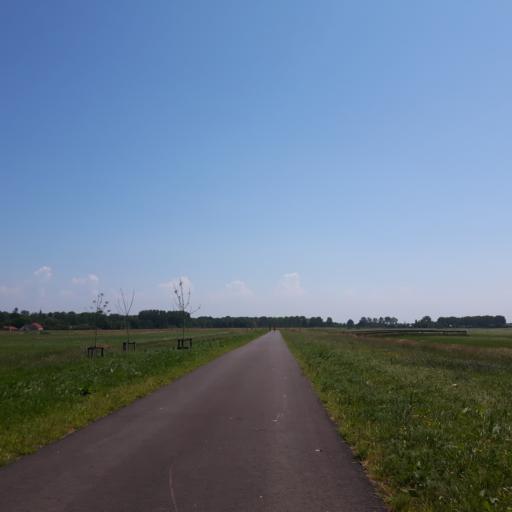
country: NL
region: Utrecht
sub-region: Stichtse Vecht
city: Spechtenkamp
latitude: 52.1286
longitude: 4.9748
